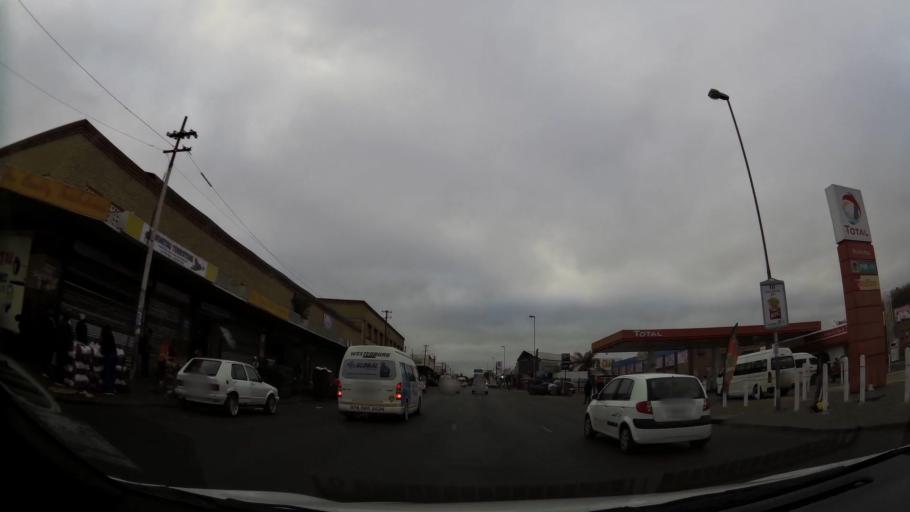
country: ZA
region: Limpopo
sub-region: Capricorn District Municipality
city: Polokwane
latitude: -23.9035
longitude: 29.4464
